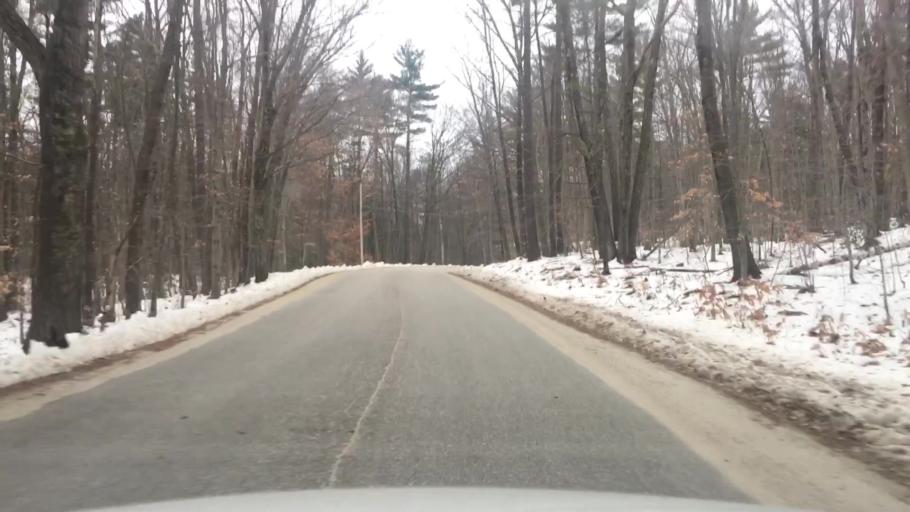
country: US
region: New Hampshire
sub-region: Merrimack County
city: Hopkinton
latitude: 43.1721
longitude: -71.6744
